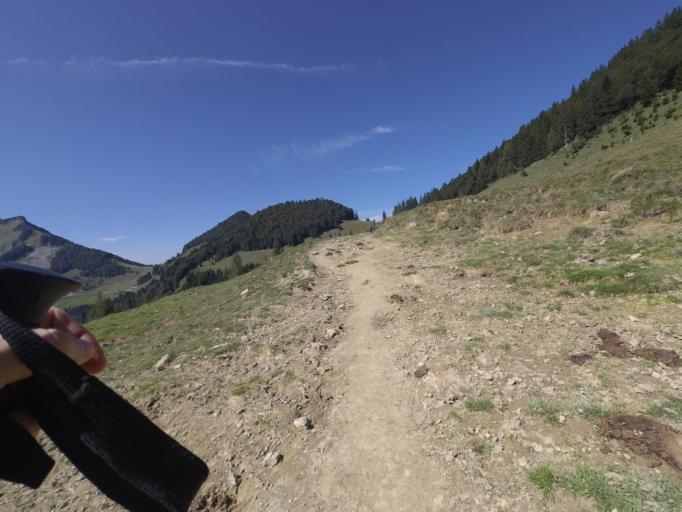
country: AT
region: Salzburg
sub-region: Politischer Bezirk Salzburg-Umgebung
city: Hintersee
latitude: 47.6848
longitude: 13.2721
